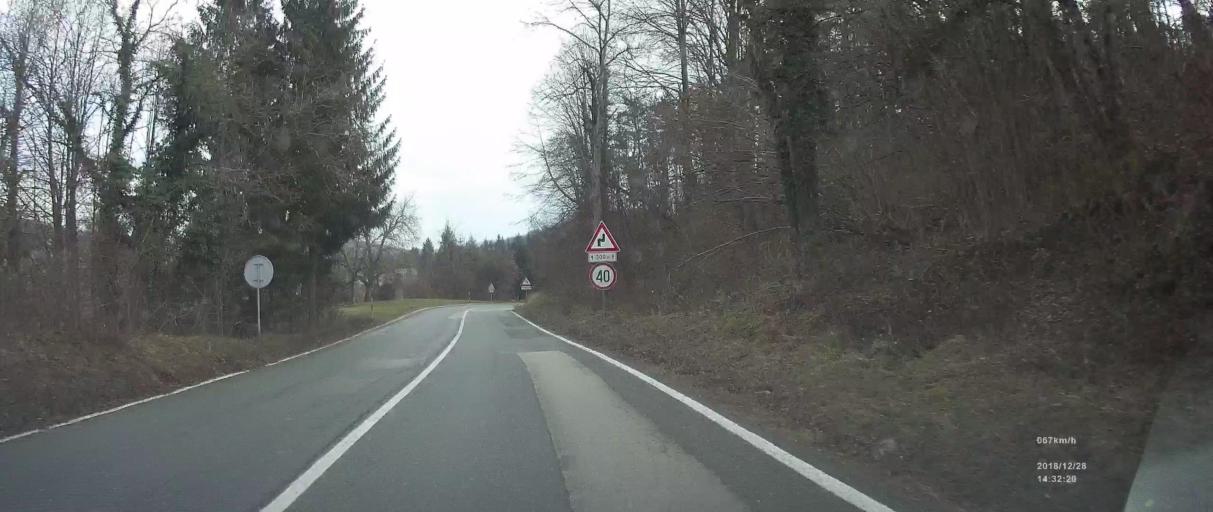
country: HR
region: Primorsko-Goranska
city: Vrbovsko
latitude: 45.4128
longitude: 15.1542
